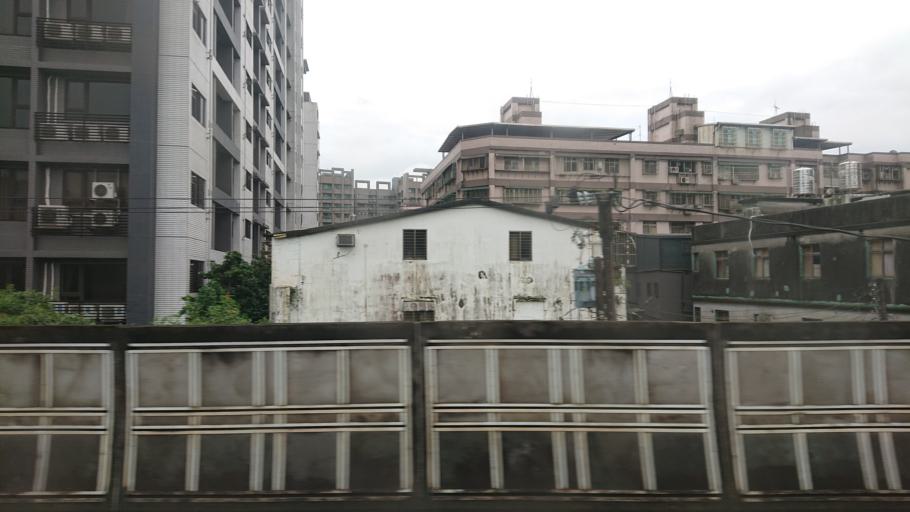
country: TW
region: Taiwan
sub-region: Keelung
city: Keelung
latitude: 25.0819
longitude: 121.6741
